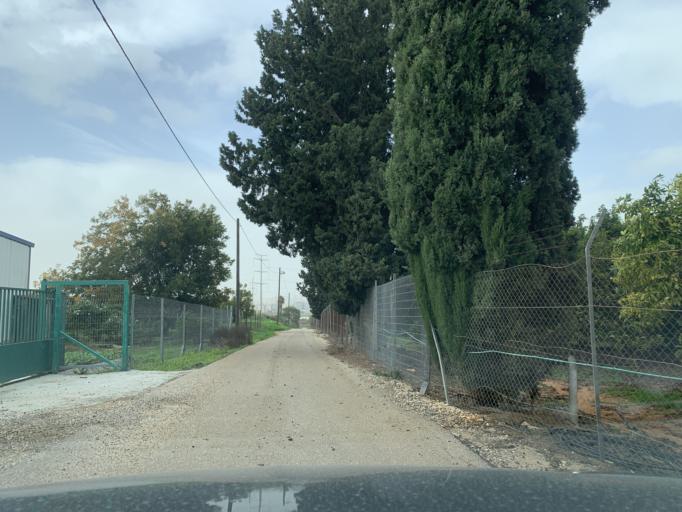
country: IL
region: Central District
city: Jaljulya
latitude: 32.1628
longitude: 34.9449
